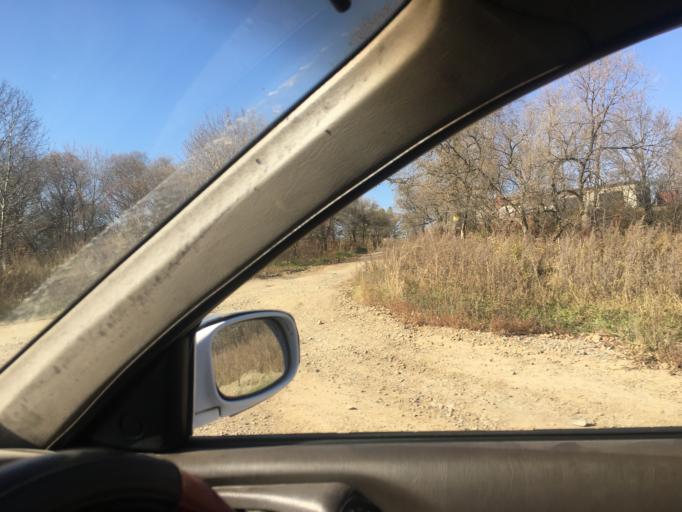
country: RU
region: Primorskiy
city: Dal'nerechensk
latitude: 45.9277
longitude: 133.7091
